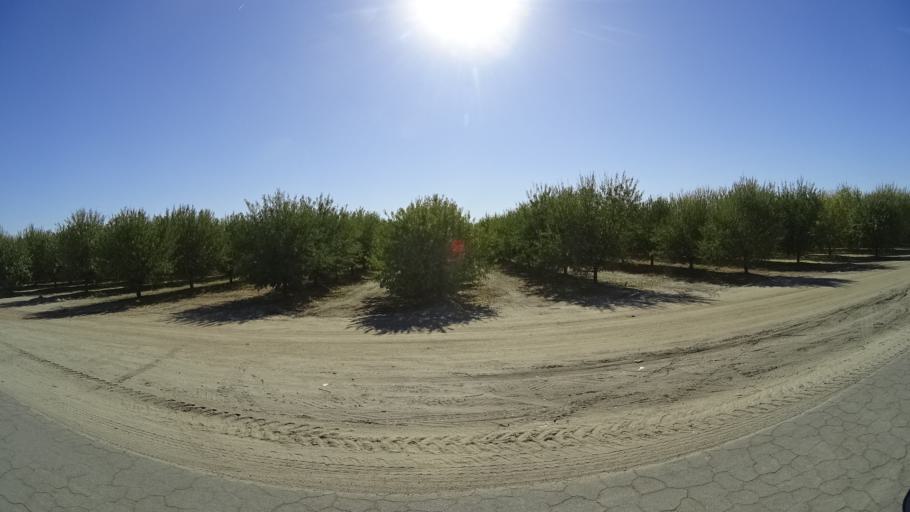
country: US
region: California
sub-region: Kern County
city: Greenfield
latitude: 35.2598
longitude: -119.0612
